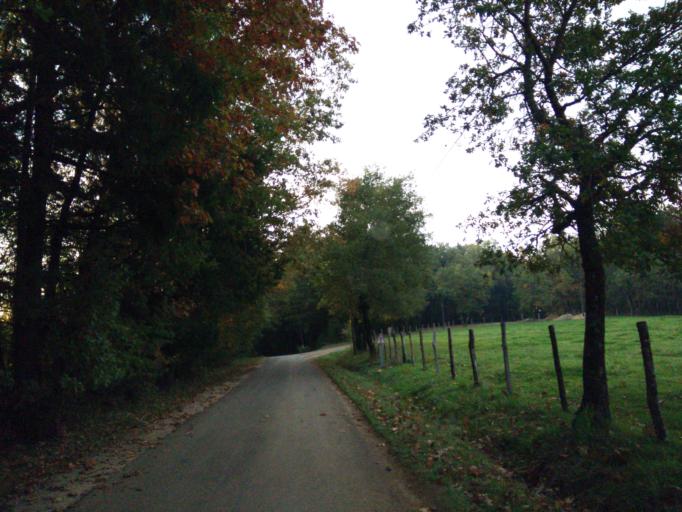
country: FR
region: Aquitaine
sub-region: Departement de la Dordogne
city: Rouffignac-Saint-Cernin-de-Reilhac
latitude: 45.0126
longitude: 0.9856
